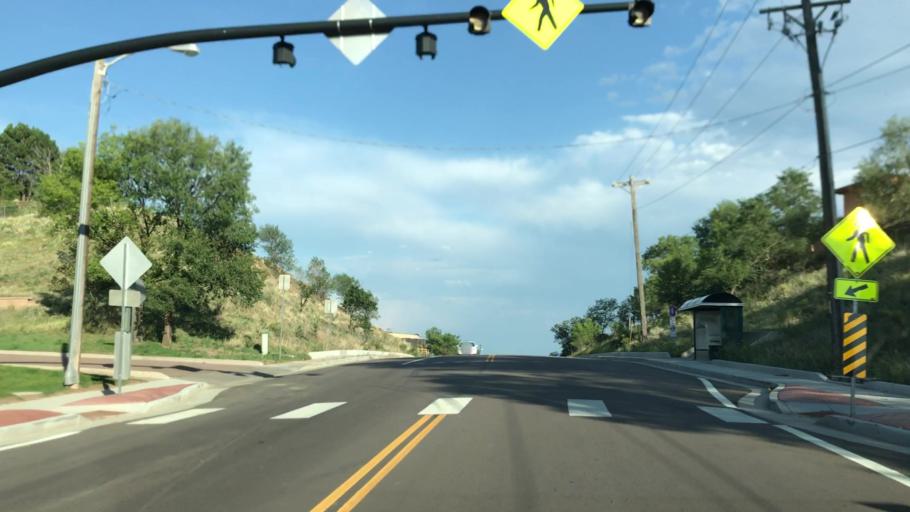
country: US
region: Colorado
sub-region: El Paso County
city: Colorado Springs
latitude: 38.8523
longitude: -104.8621
